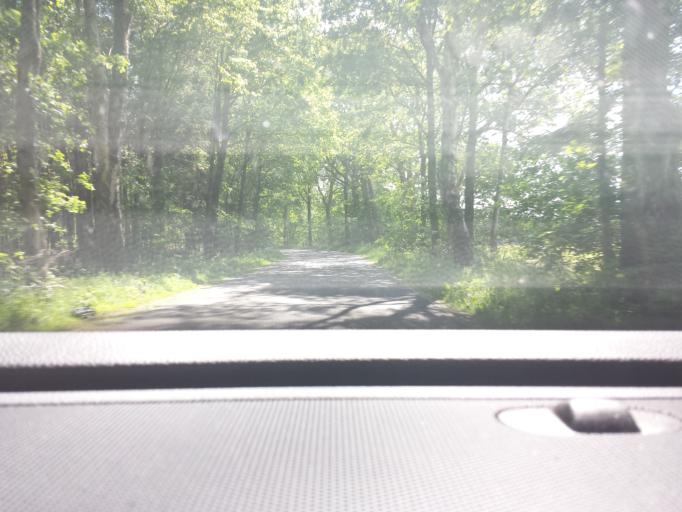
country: NL
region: Gelderland
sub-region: Gemeente Lochem
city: Almen
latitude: 52.1340
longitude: 6.3145
